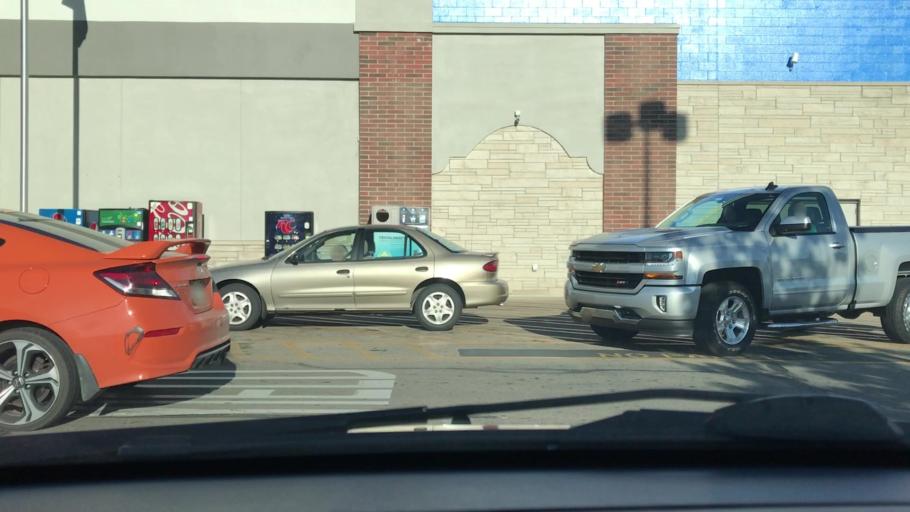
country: US
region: Indiana
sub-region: Madison County
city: Anderson
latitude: 40.0644
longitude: -85.6505
